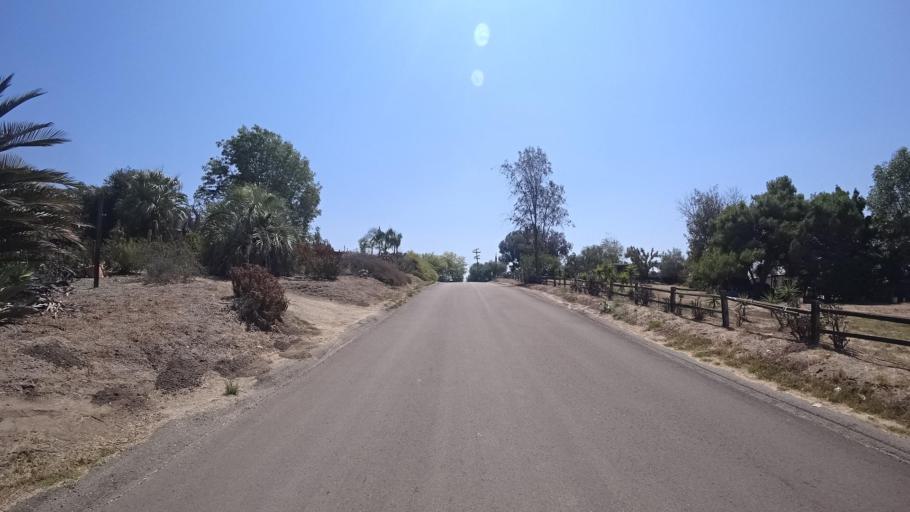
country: US
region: California
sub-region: San Diego County
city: Vista
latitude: 33.1777
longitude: -117.2548
